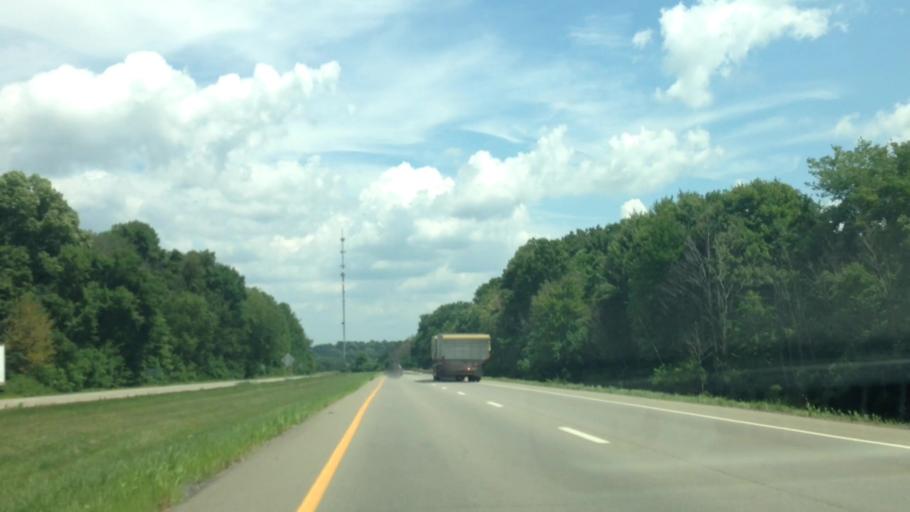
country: US
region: Ohio
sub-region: Wayne County
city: Doylestown
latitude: 40.9813
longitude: -81.6934
